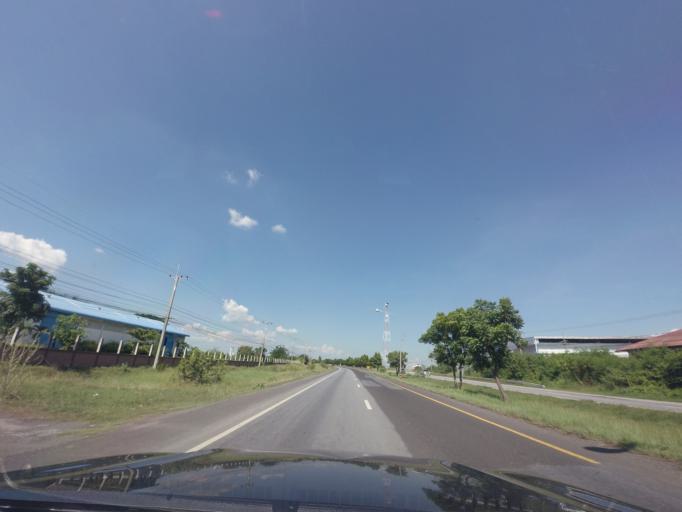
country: TH
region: Nakhon Ratchasima
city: Non Sung
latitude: 15.1885
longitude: 102.3445
